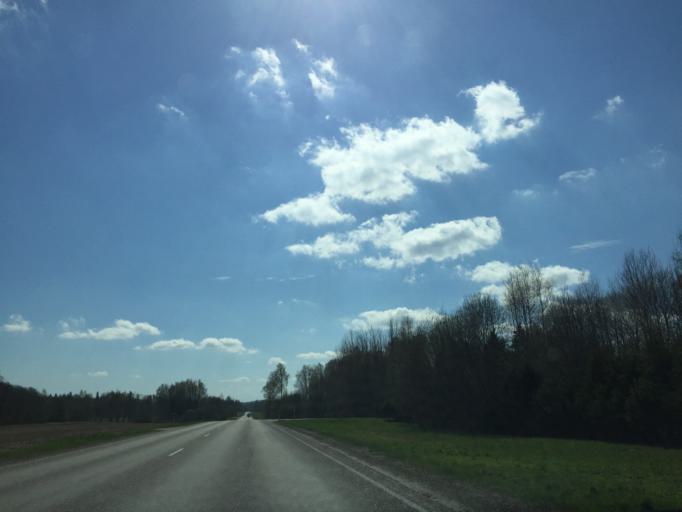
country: EE
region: Tartu
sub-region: Elva linn
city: Elva
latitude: 58.1038
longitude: 26.2346
